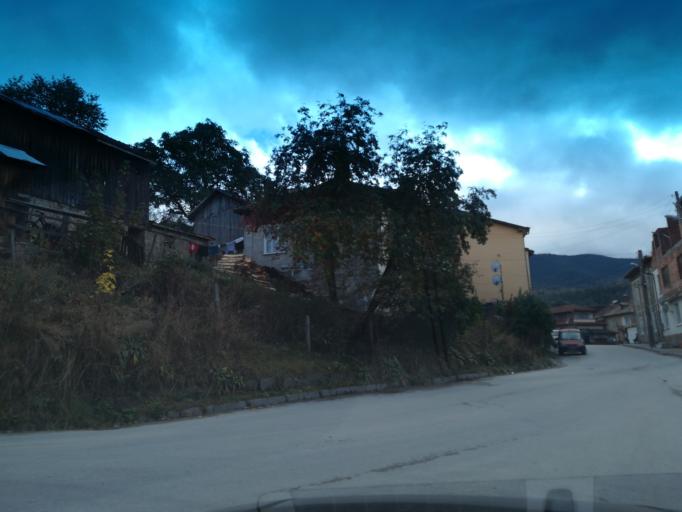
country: BG
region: Pazardzhik
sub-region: Obshtina Batak
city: Batak
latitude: 41.9357
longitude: 24.2692
